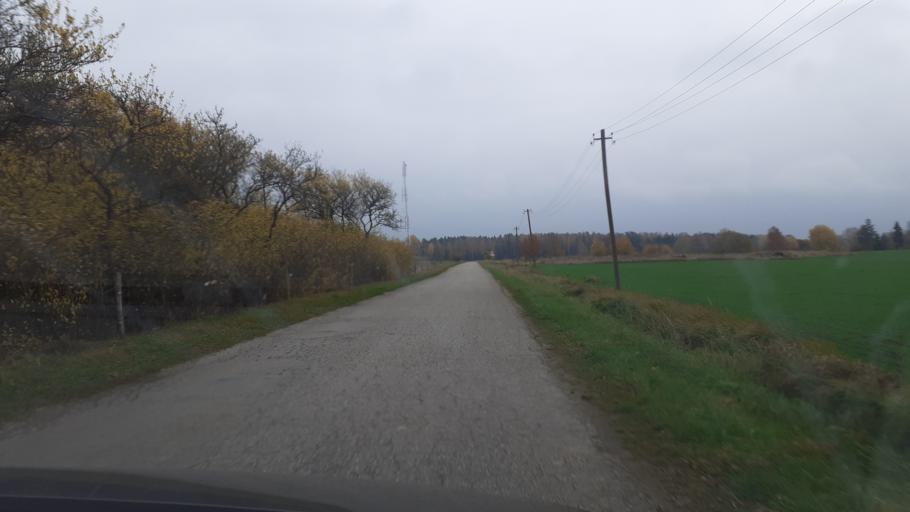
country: LV
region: Skrunda
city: Skrunda
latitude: 56.8572
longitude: 22.2325
